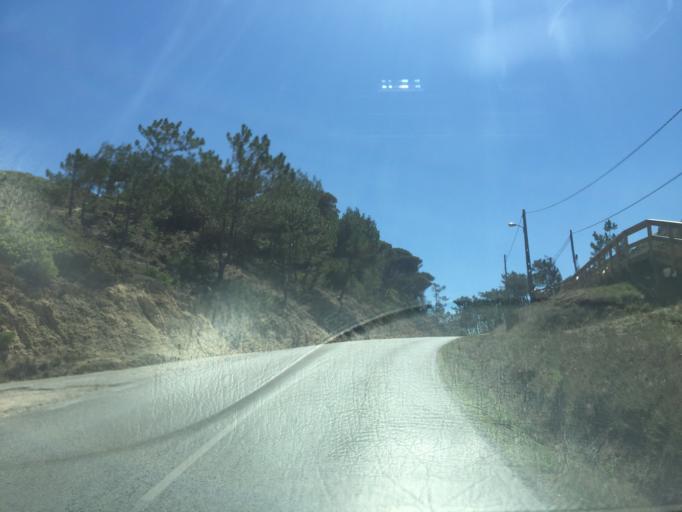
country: PT
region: Lisbon
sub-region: Torres Vedras
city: A dos Cunhados
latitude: 39.1801
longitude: -9.3459
